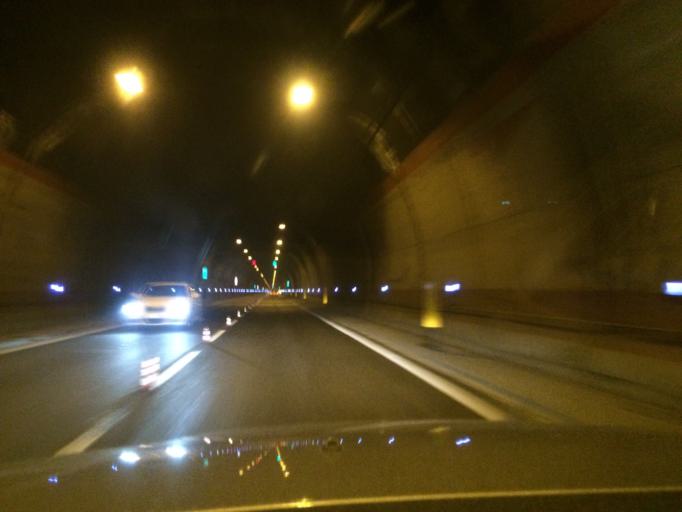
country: IT
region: Umbria
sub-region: Provincia di Terni
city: San Gemini
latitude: 42.6341
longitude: 12.5465
